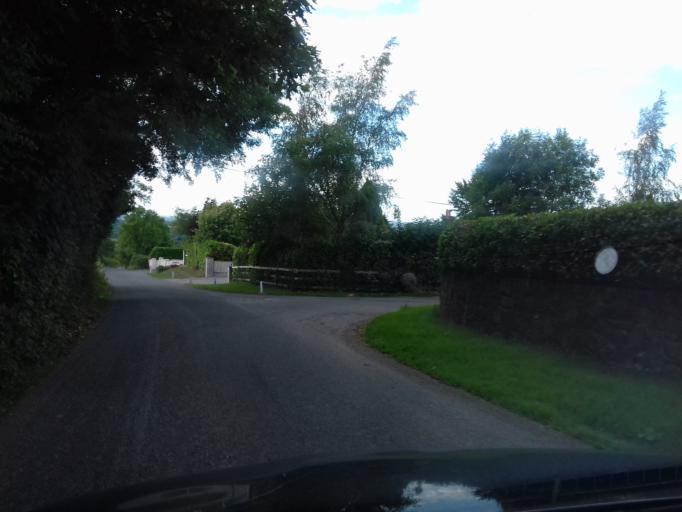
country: IE
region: Leinster
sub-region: Kilkenny
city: Graiguenamanagh
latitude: 52.5798
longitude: -7.0132
